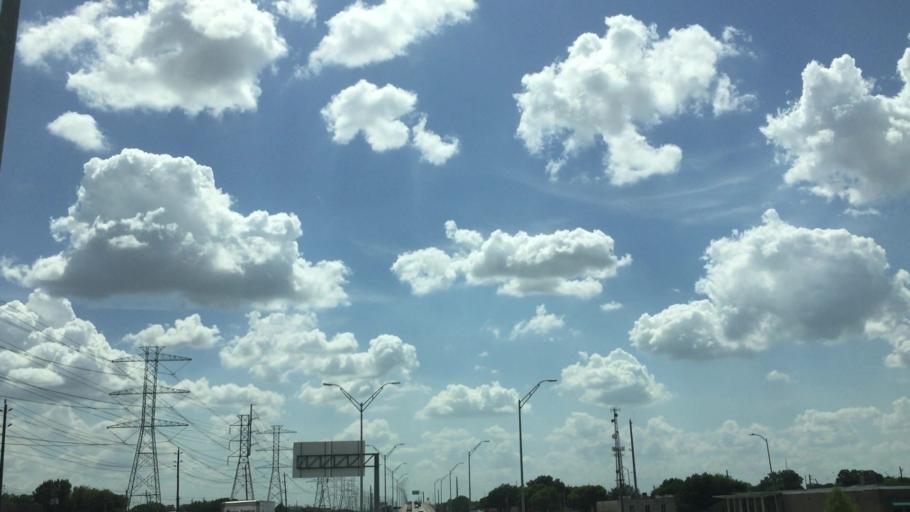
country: US
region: Texas
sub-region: Harris County
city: Piney Point Village
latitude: 29.7226
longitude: -95.5044
